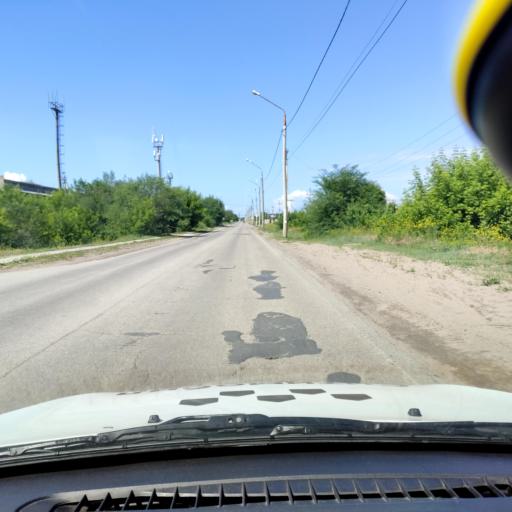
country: RU
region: Samara
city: Zhigulevsk
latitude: 53.4648
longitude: 49.5935
